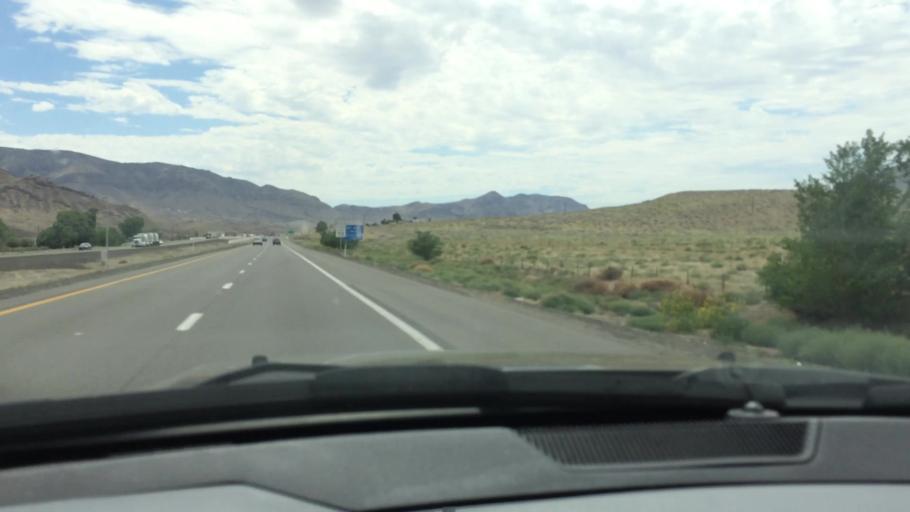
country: US
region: Nevada
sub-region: Lyon County
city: Fernley
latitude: 39.6127
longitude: -119.3161
